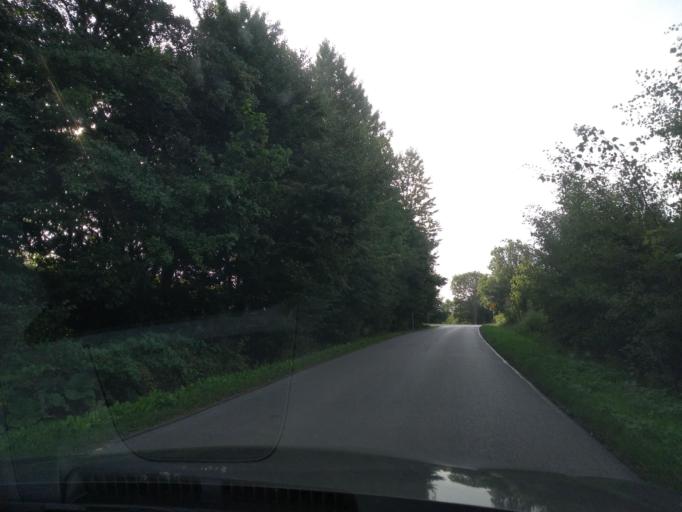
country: PL
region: Subcarpathian Voivodeship
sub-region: Powiat brzozowski
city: Dydnia
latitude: 49.6523
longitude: 22.2278
